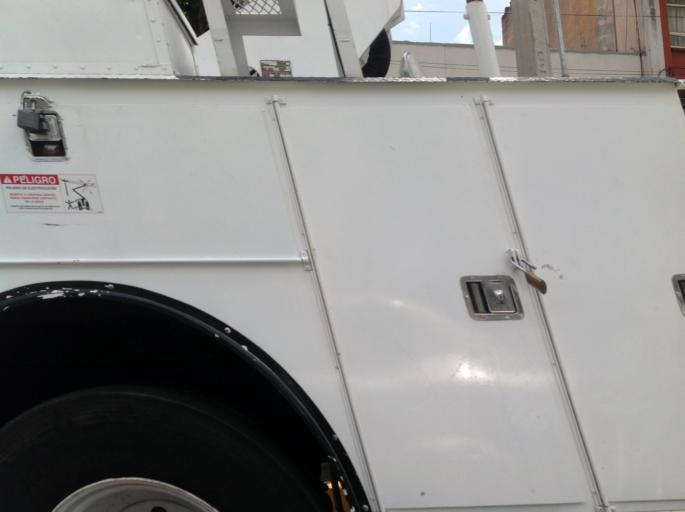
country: MX
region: Mexico City
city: Azcapotzalco
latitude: 19.4694
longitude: -99.1868
